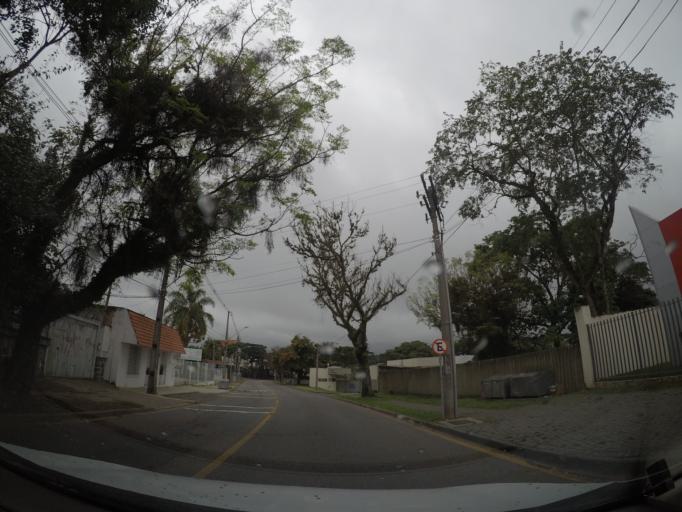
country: BR
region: Parana
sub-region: Curitiba
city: Curitiba
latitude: -25.4481
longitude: -49.3120
